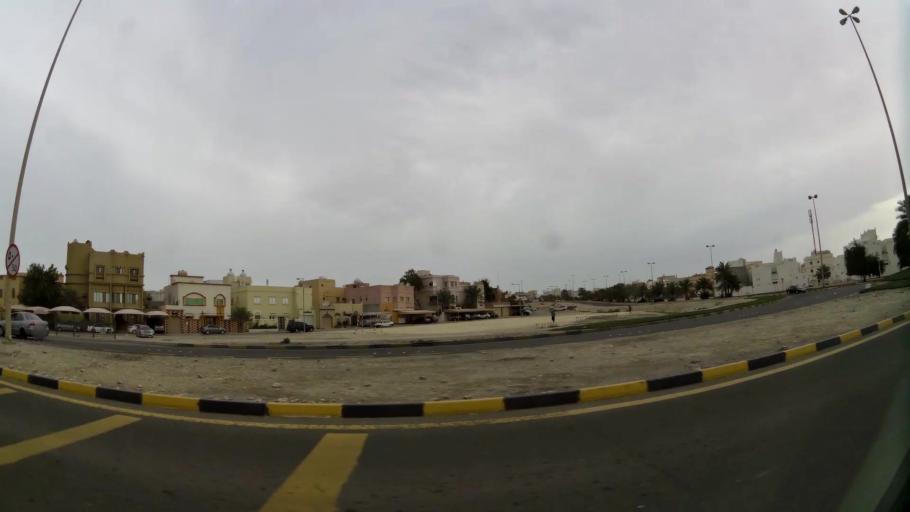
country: BH
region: Central Governorate
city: Madinat Hamad
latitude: 26.1036
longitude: 50.4981
